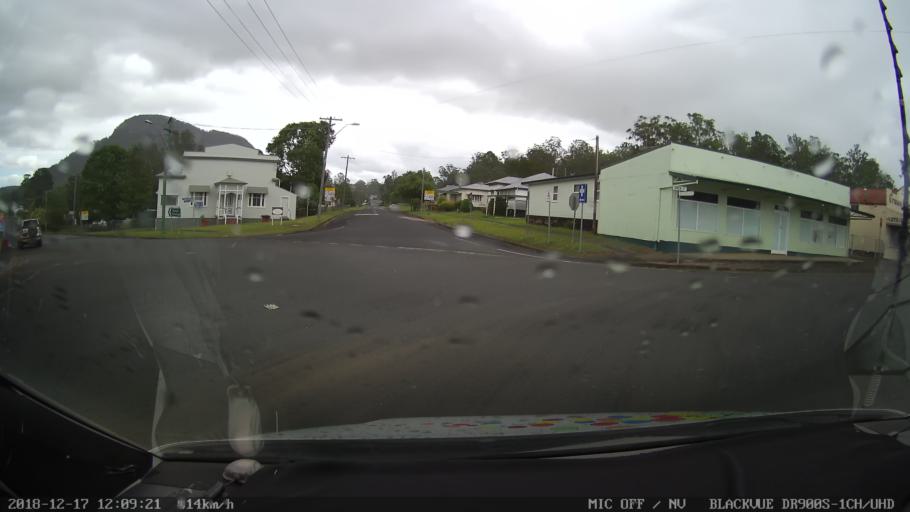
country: AU
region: New South Wales
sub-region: Kyogle
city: Kyogle
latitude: -28.4730
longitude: 152.5480
